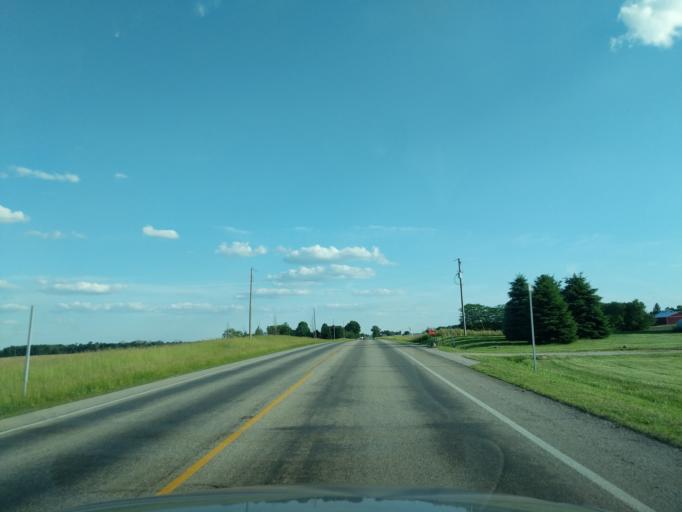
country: US
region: Indiana
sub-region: Huntington County
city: Roanoke
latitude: 40.9807
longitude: -85.4715
